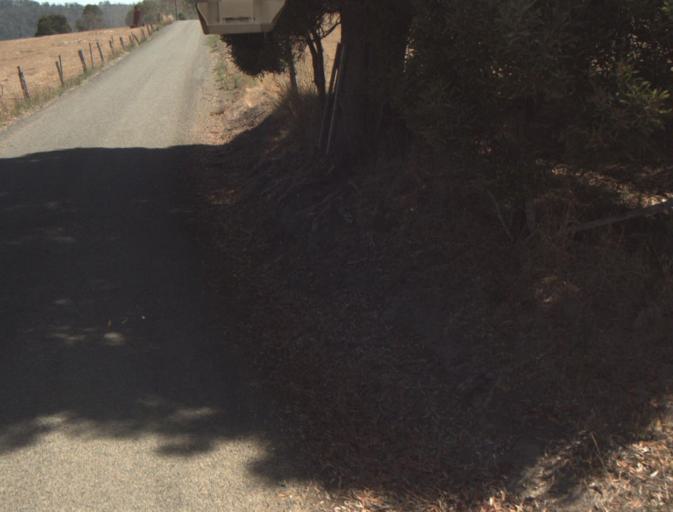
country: AU
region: Tasmania
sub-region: Launceston
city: Mayfield
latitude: -41.2553
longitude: 147.1862
